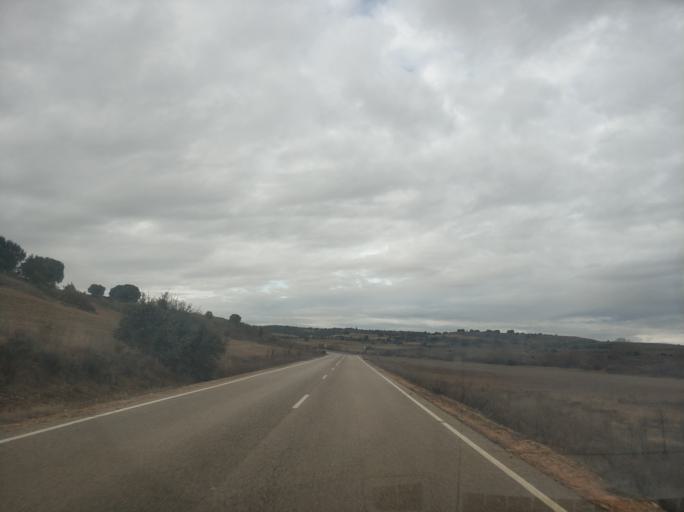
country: ES
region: Castille and Leon
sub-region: Provincia de Soria
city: Alcubilla de Avellaneda
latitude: 41.7537
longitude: -3.2741
